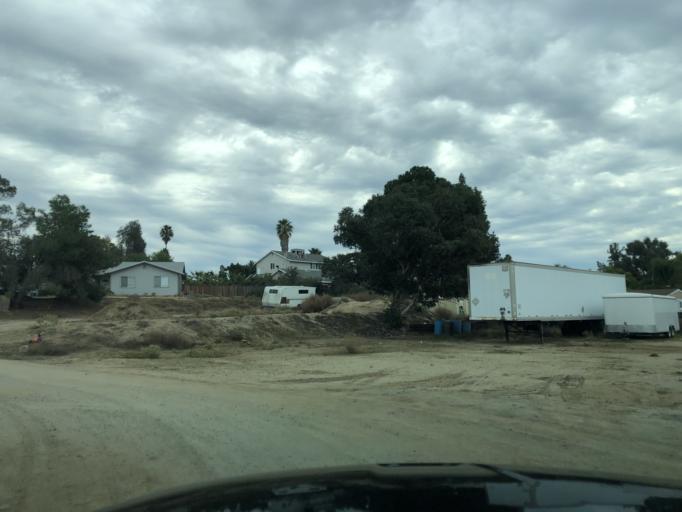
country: US
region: California
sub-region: Riverside County
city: Wildomar
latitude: 33.6218
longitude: -117.2786
